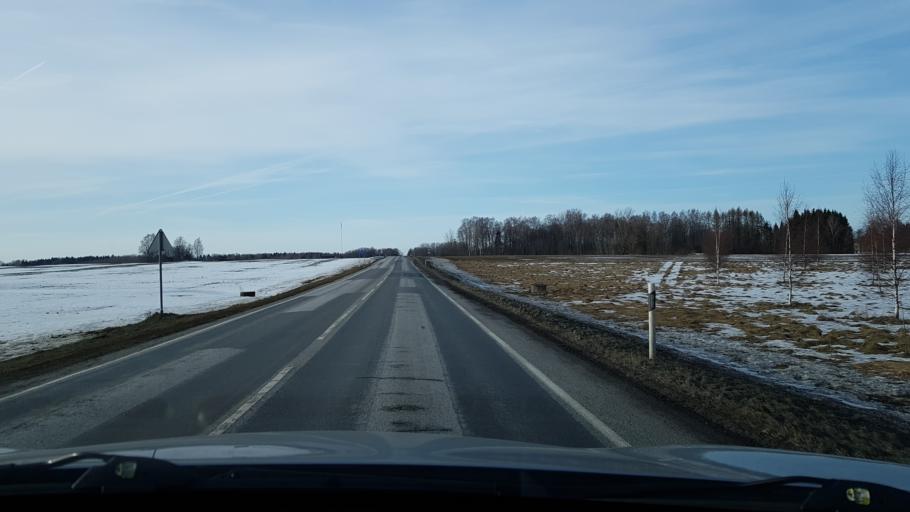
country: EE
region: Viljandimaa
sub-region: Viljandi linn
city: Viljandi
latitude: 58.3549
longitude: 25.4382
